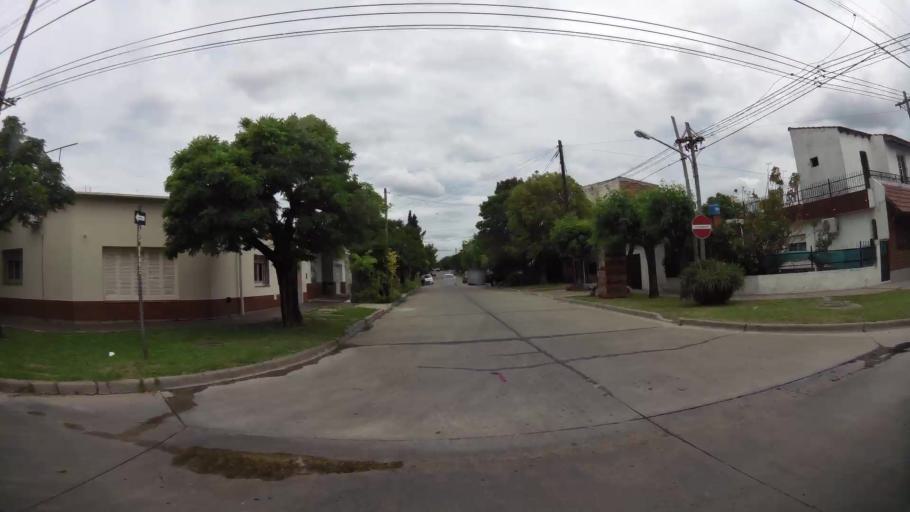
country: AR
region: Buenos Aires
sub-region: Partido de Campana
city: Campana
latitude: -34.1693
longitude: -58.9700
